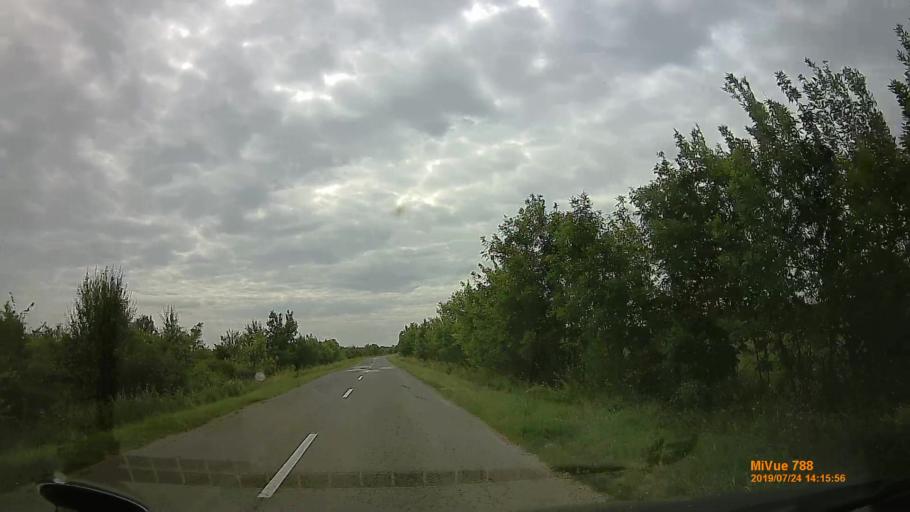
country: UA
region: Zakarpattia
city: Batiovo
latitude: 48.3194
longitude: 22.3007
